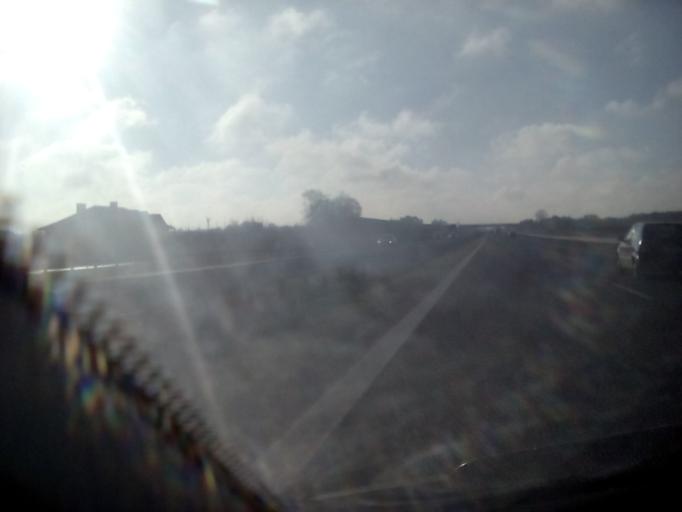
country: PL
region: Masovian Voivodeship
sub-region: Powiat grojecki
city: Jasieniec
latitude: 51.8046
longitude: 20.8876
